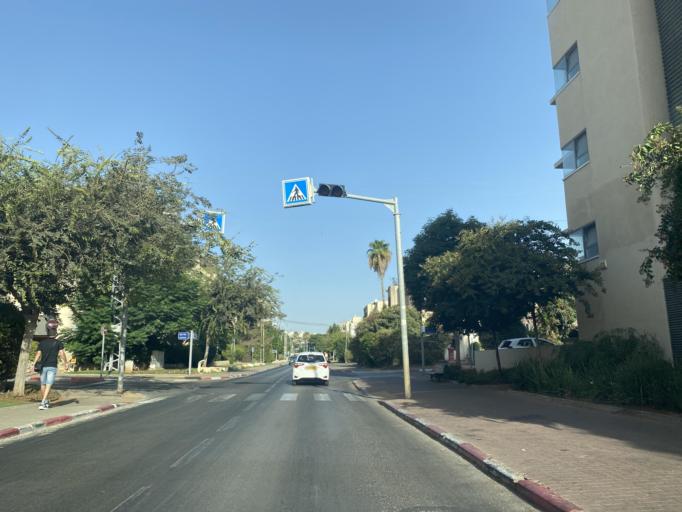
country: IL
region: Tel Aviv
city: Ramat HaSharon
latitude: 32.1648
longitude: 34.8457
